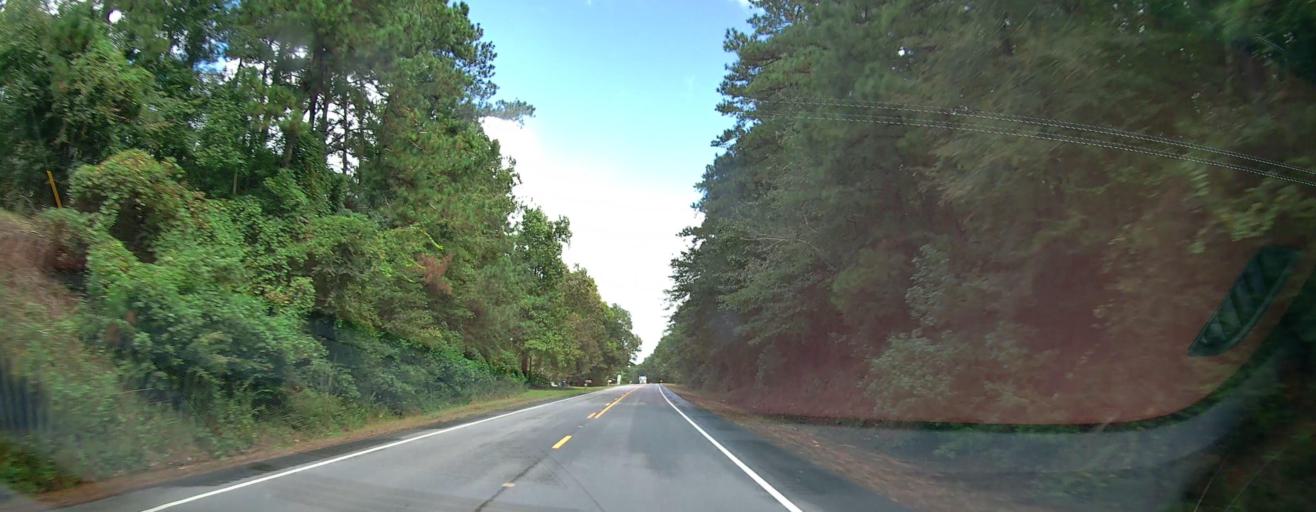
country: US
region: Georgia
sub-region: Baldwin County
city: Milledgeville
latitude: 33.0212
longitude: -83.3339
